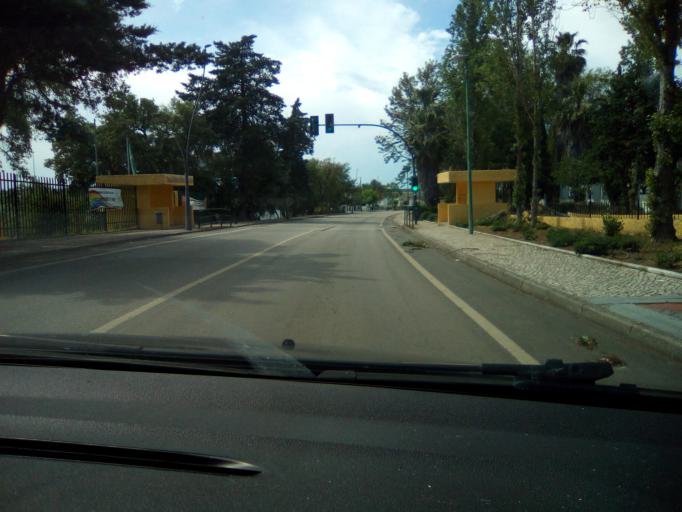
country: PT
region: Portalegre
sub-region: Avis
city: Avis
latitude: 39.0528
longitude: -7.8934
